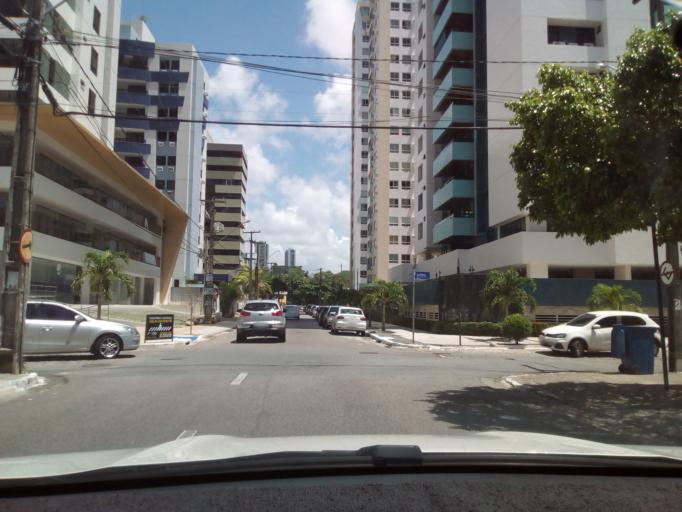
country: BR
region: Paraiba
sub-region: Joao Pessoa
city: Joao Pessoa
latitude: -7.1153
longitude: -34.8292
